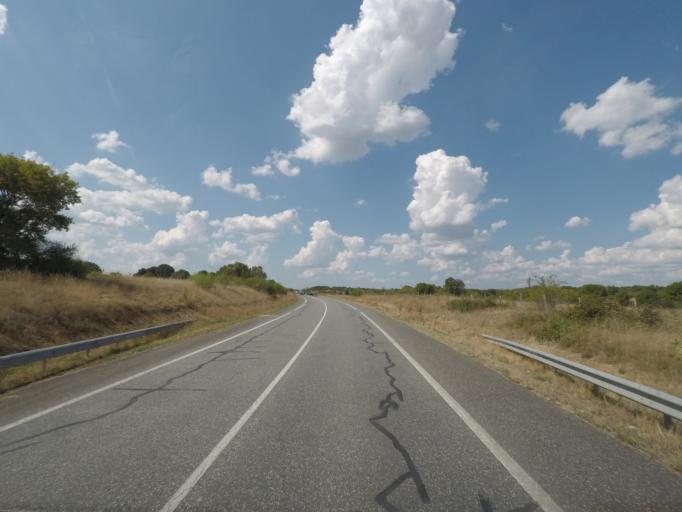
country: FR
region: Midi-Pyrenees
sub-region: Departement du Lot
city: Gramat
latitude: 44.6907
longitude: 1.5987
